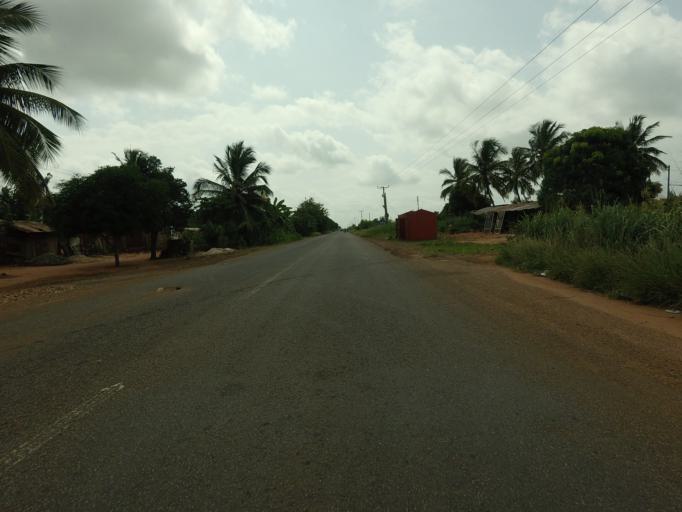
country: TG
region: Maritime
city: Lome
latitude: 6.1757
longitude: 1.0709
